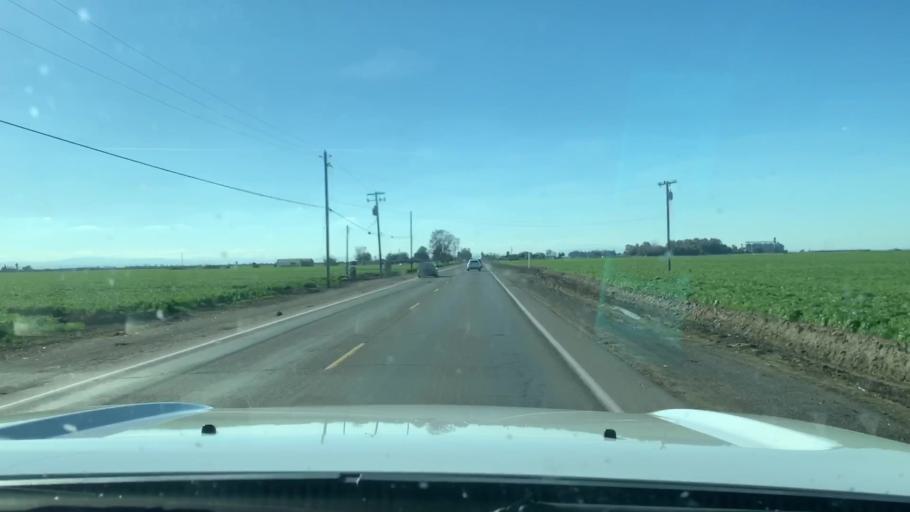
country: US
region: California
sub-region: Kings County
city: Home Garden
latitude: 36.2112
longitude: -119.6225
